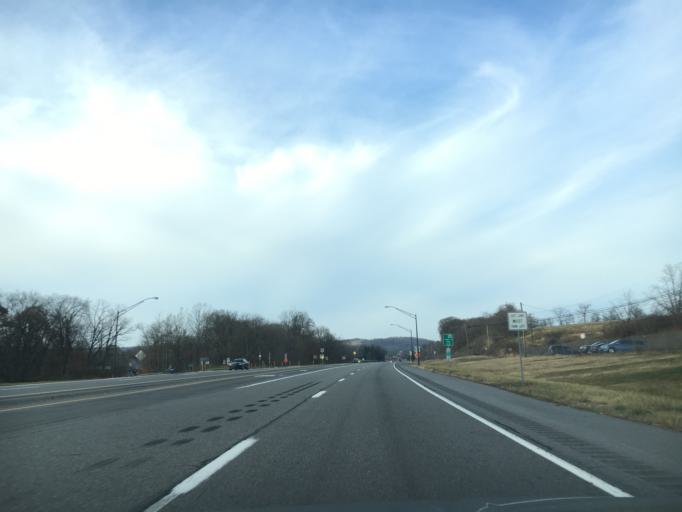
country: US
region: Pennsylvania
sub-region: Montour County
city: Danville
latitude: 40.9853
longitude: -76.6307
